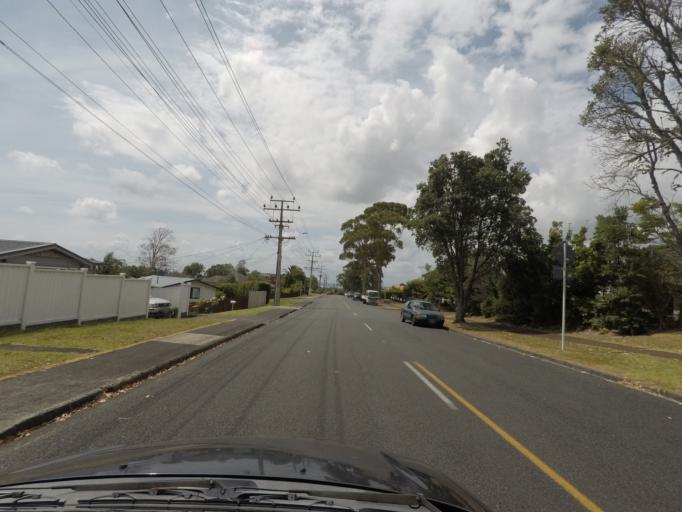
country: NZ
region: Auckland
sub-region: Auckland
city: Waitakere
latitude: -36.9000
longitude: 174.6424
